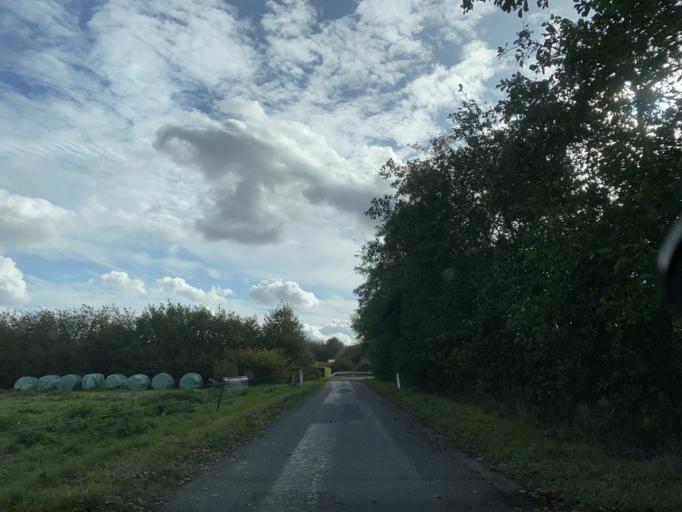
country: DK
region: Central Jutland
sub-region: Arhus Kommune
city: Sabro
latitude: 56.2096
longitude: 9.9988
